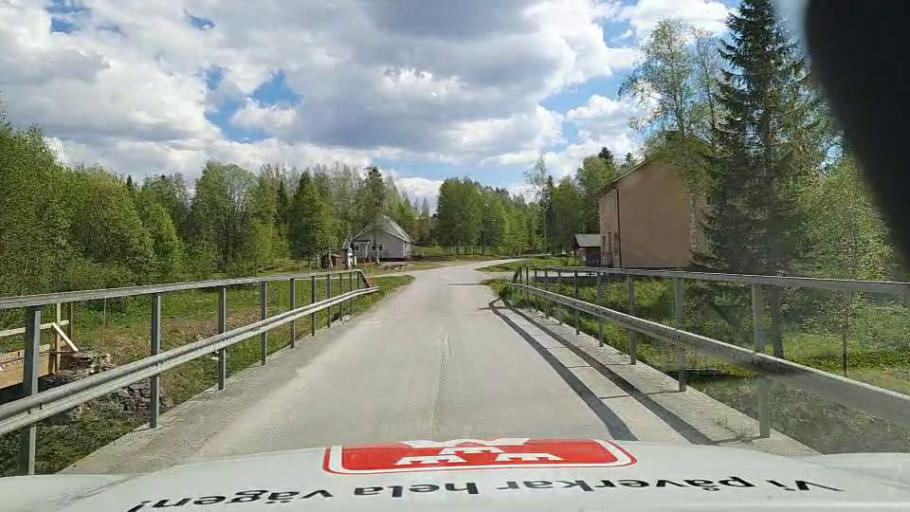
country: NO
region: Nord-Trondelag
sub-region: Lierne
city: Sandvika
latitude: 64.1217
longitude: 14.1374
